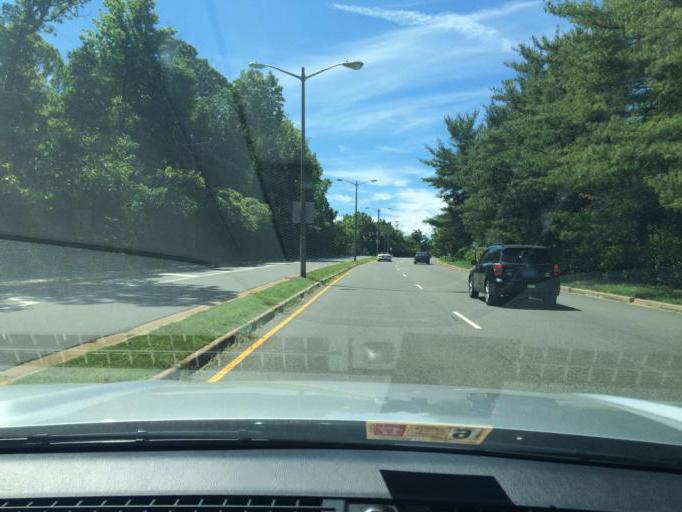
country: US
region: Virginia
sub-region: Fairfax County
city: Baileys Crossroads
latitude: 38.8378
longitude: -77.0847
